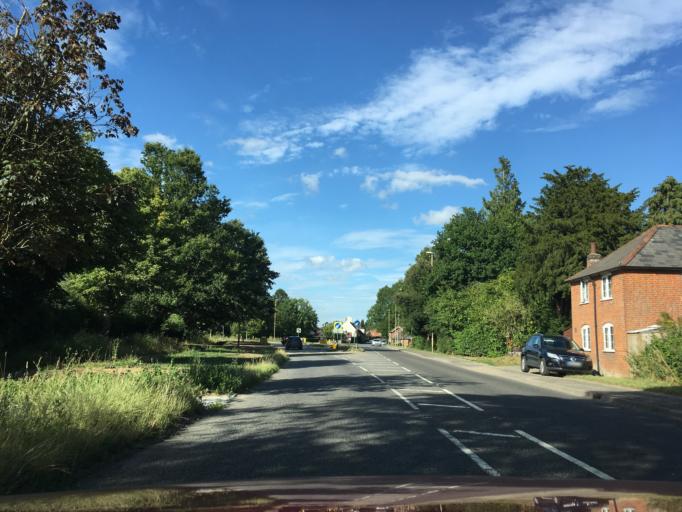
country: GB
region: England
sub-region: Hampshire
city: Romsey
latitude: 50.9826
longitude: -1.5071
